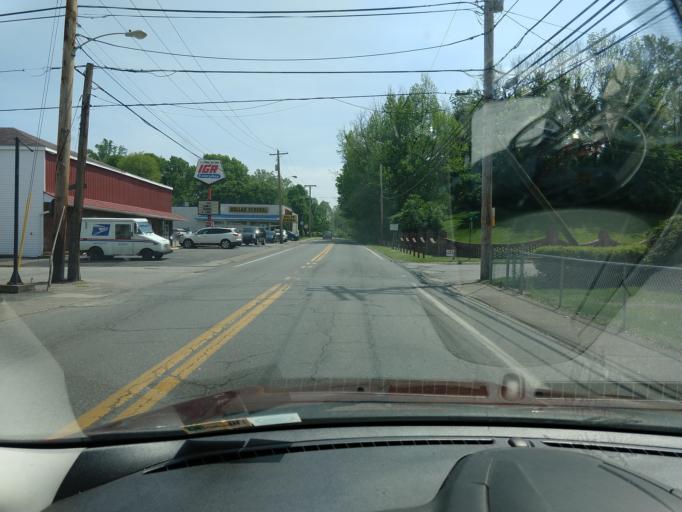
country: US
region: West Virginia
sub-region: Kanawha County
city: Saint Albans
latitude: 38.3770
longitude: -81.8058
